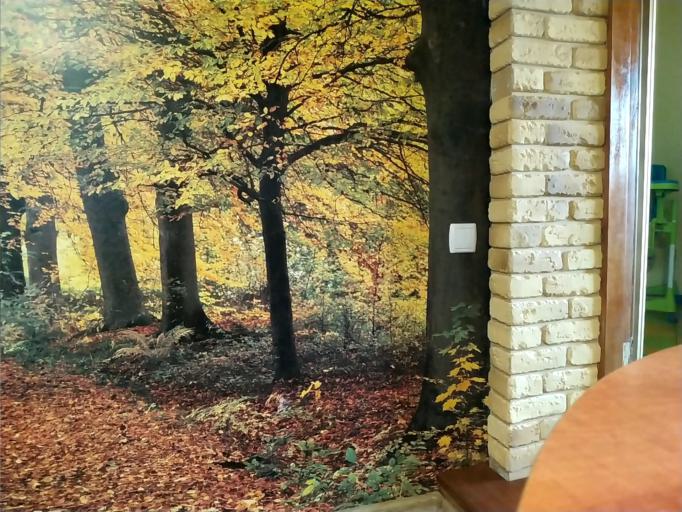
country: RU
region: Leningrad
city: Tolmachevo
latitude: 58.9478
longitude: 29.6435
